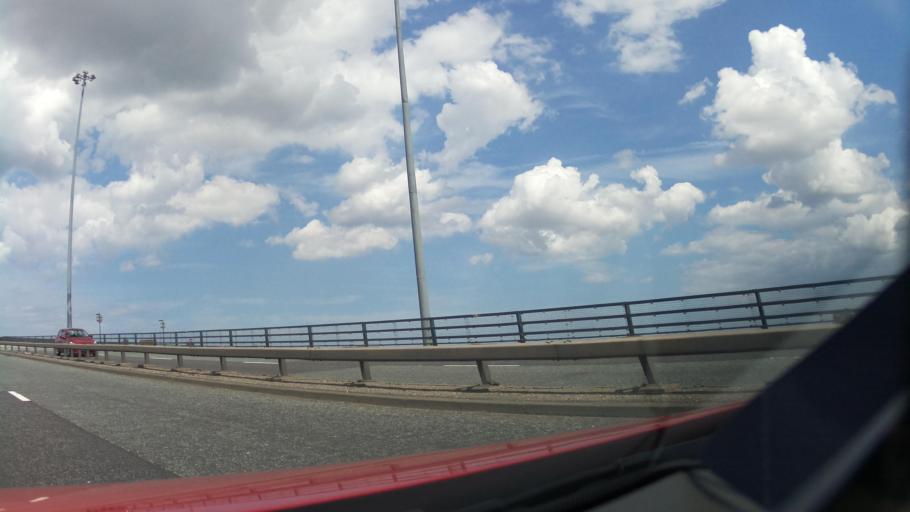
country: GB
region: England
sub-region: Stockton-on-Tees
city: Billingham
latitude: 54.5643
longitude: -1.2671
